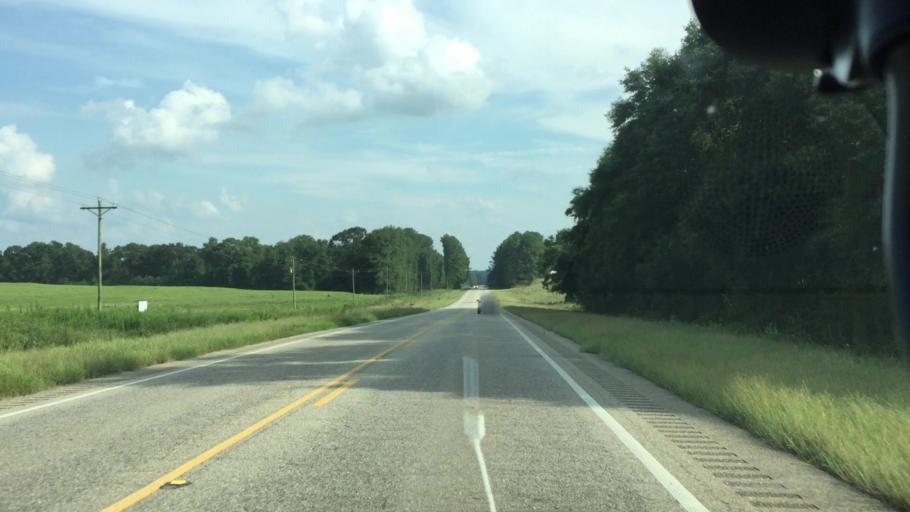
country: US
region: Alabama
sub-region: Pike County
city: Brundidge
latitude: 31.6532
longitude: -85.9506
